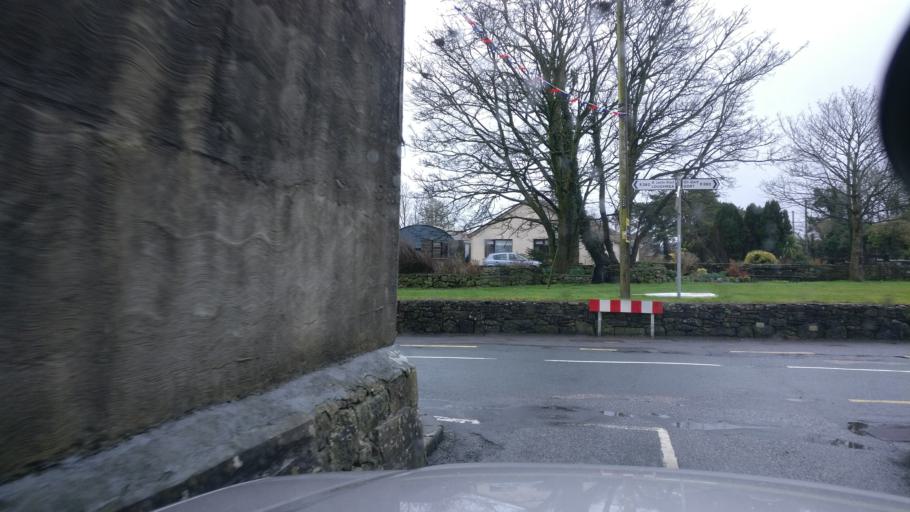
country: IE
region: Connaught
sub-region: County Galway
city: Loughrea
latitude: 53.1786
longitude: -8.6529
